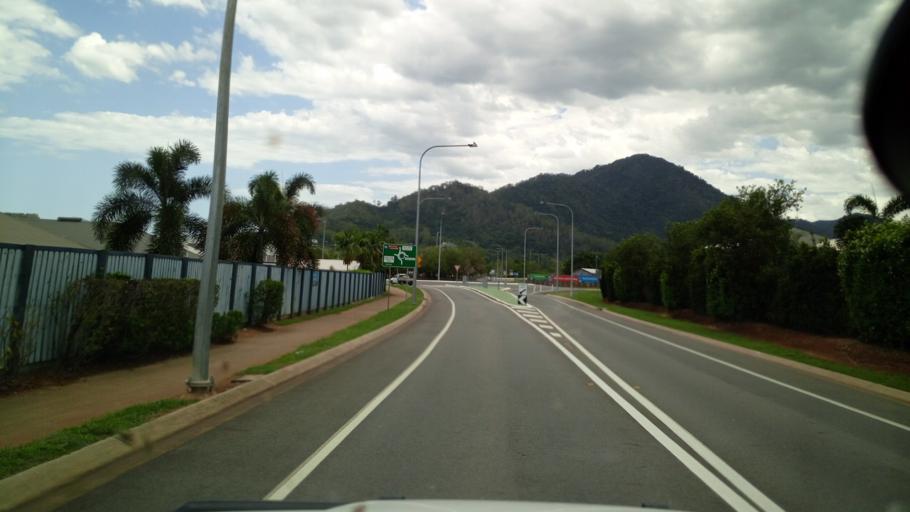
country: AU
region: Queensland
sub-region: Cairns
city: Redlynch
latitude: -16.8995
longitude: 145.6974
